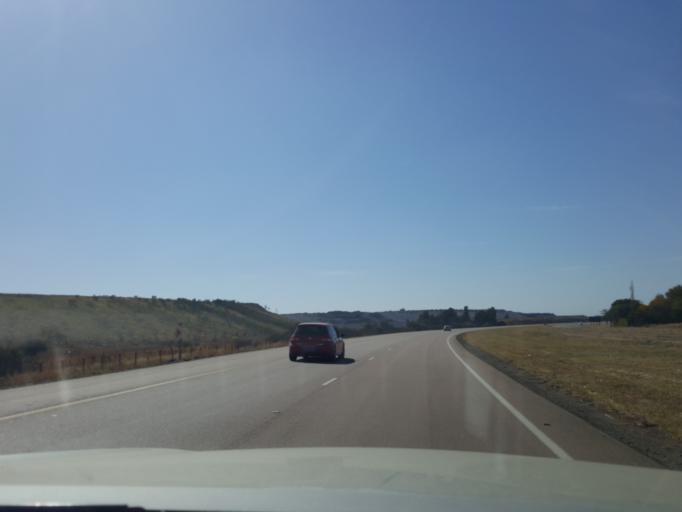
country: ZA
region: North-West
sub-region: Bojanala Platinum District Municipality
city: Rustenburg
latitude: -25.7484
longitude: 27.5061
